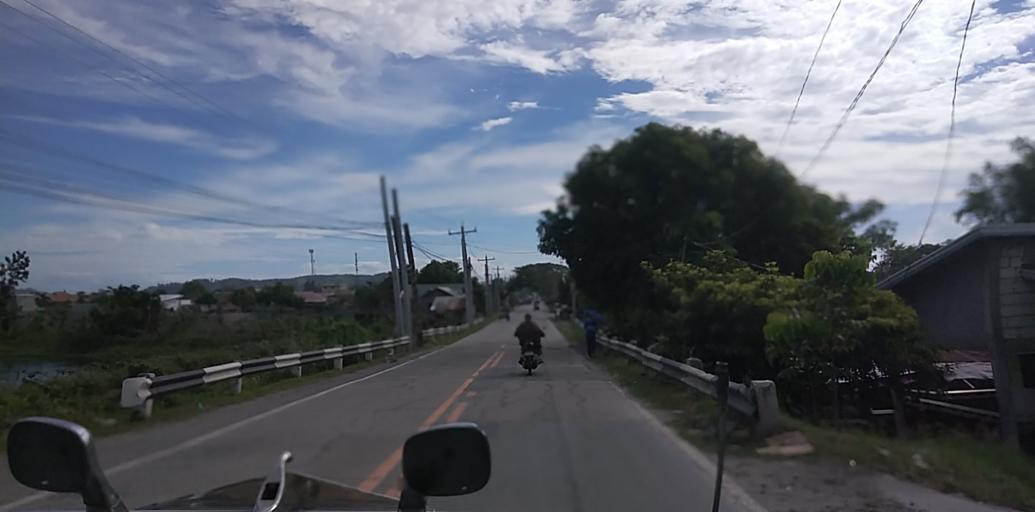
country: PH
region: Central Luzon
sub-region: Province of Pampanga
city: Anao
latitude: 15.1551
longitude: 120.7200
